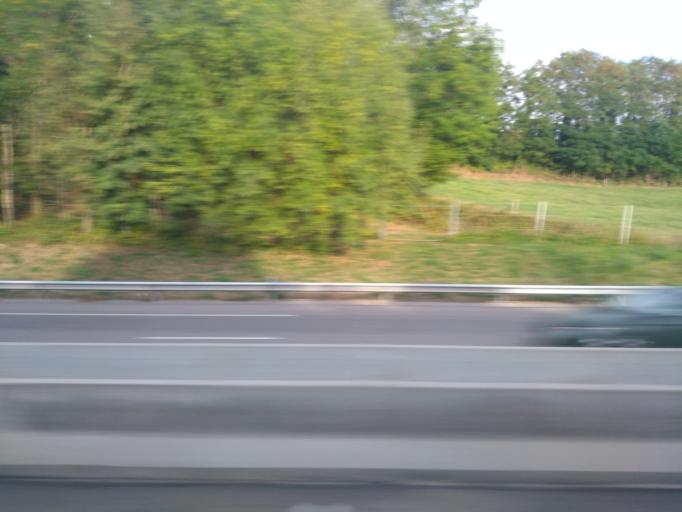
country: FR
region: Rhone-Alpes
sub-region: Departement de l'Isere
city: Chabons
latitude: 45.4645
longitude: 5.4014
